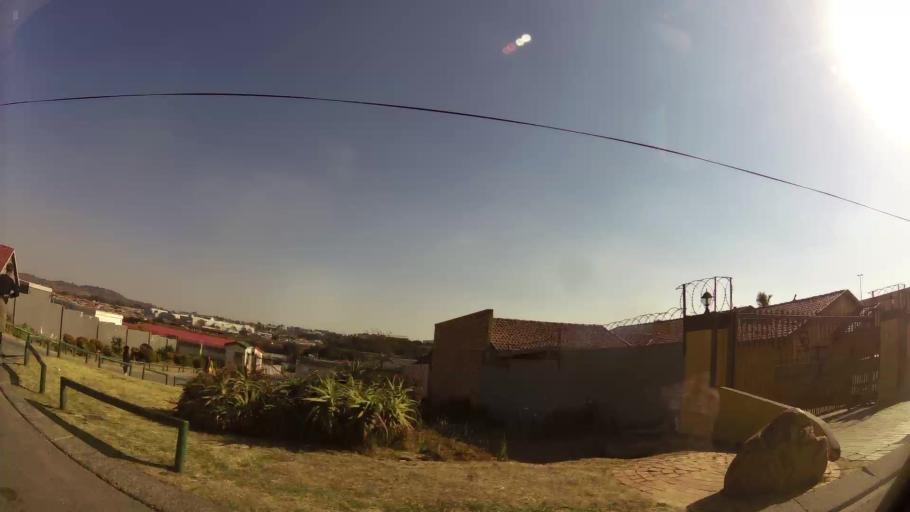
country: ZA
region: Gauteng
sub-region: City of Johannesburg Metropolitan Municipality
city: Johannesburg
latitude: -26.2593
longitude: 27.9890
